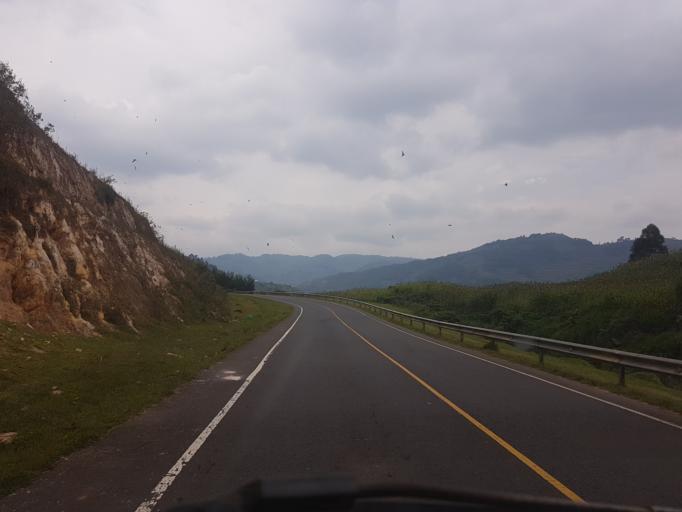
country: UG
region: Western Region
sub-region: Kabale District
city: Kabale
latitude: -1.2109
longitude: 29.8319
